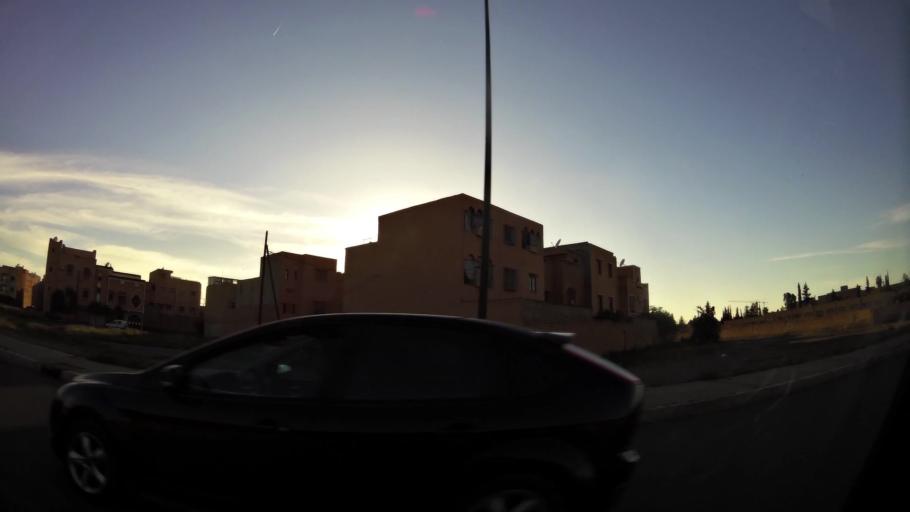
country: MA
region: Marrakech-Tensift-Al Haouz
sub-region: Marrakech
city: Marrakesh
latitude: 31.6200
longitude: -8.0443
